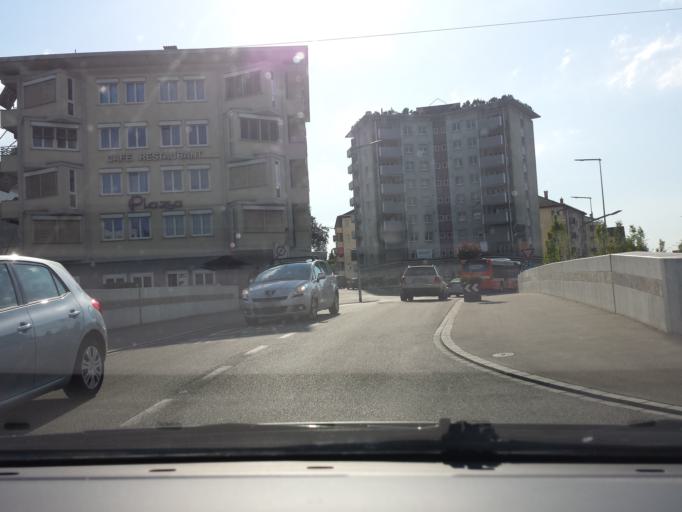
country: CH
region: Thurgau
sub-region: Arbon District
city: Arbon
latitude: 47.5163
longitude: 9.4329
